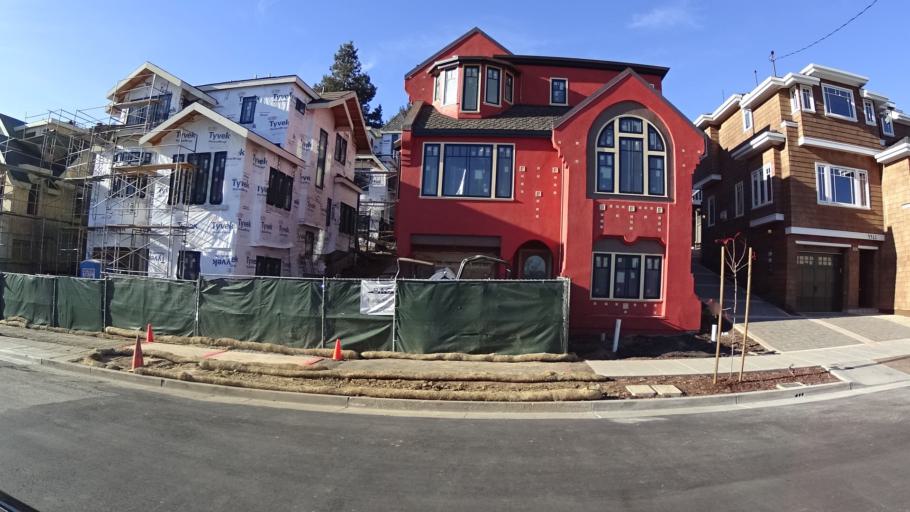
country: US
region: California
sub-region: Alameda County
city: Piedmont
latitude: 37.8317
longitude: -122.2470
